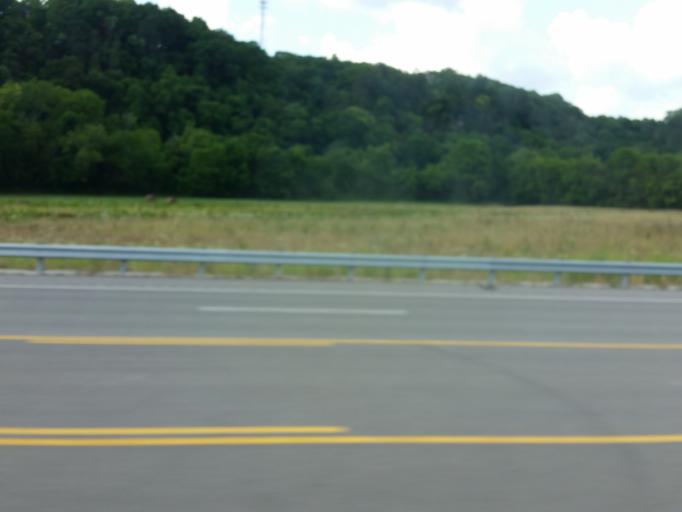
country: US
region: Tennessee
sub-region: Lewis County
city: Hohenwald
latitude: 35.5621
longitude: -87.3955
